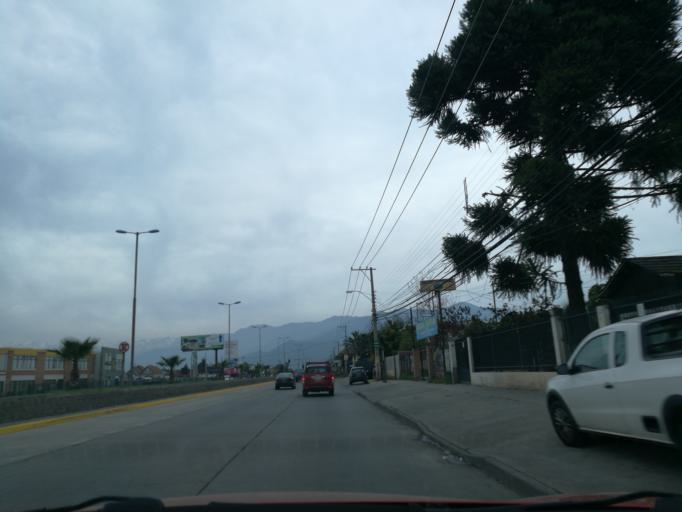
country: CL
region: O'Higgins
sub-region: Provincia de Cachapoal
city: Machali
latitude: -34.1744
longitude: -70.6905
